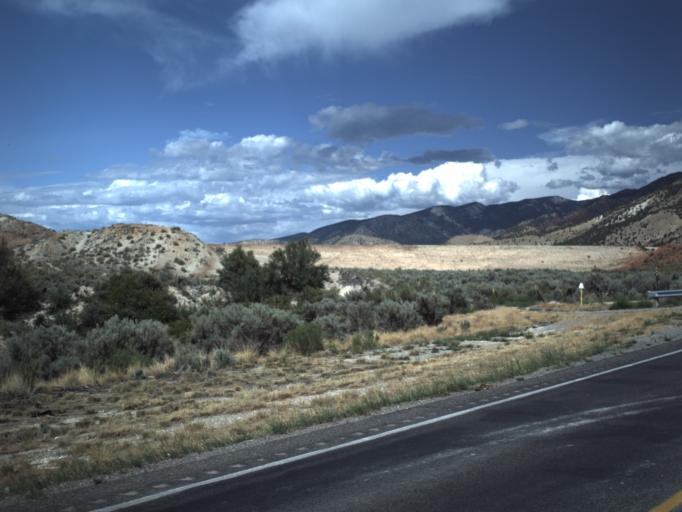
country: US
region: Utah
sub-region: Sanpete County
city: Gunnison
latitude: 39.1684
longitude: -111.7193
